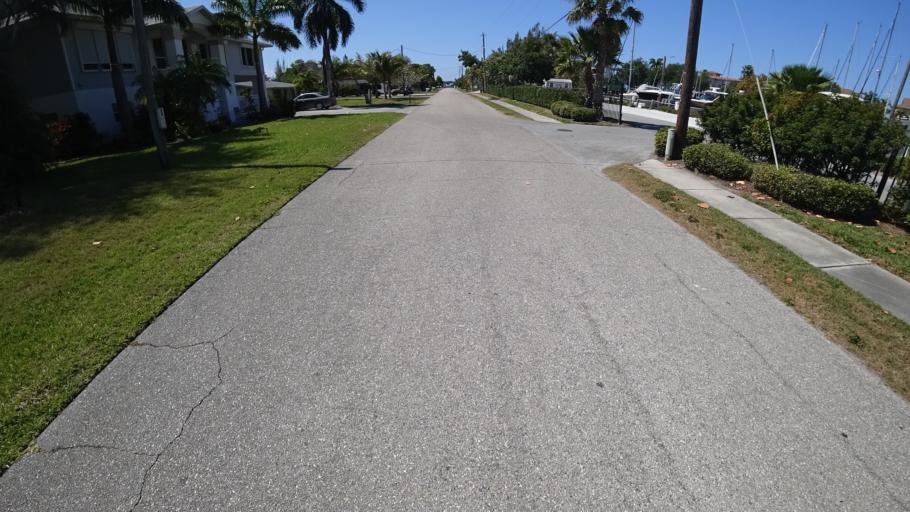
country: US
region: Florida
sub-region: Manatee County
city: Cortez
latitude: 27.4745
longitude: -82.6903
